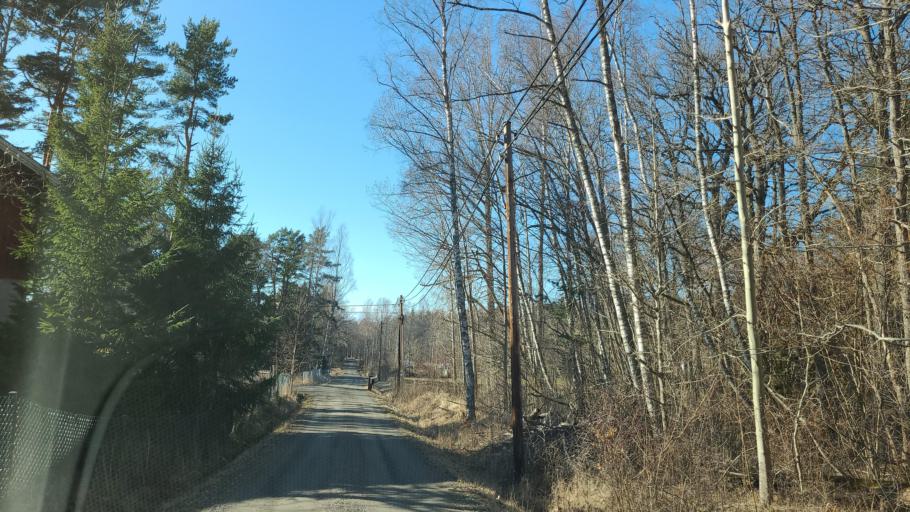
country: SE
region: Stockholm
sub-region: Varmdo Kommun
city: Holo
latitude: 59.3620
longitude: 18.6651
